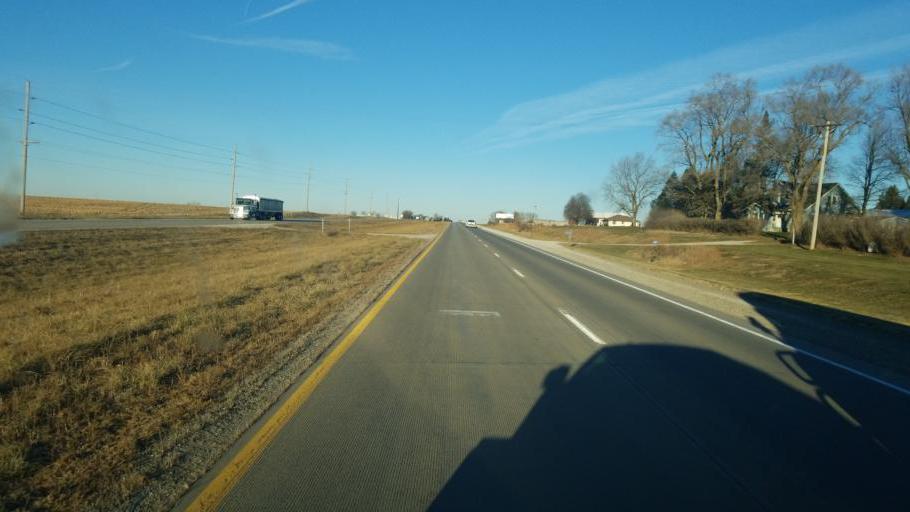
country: US
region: Iowa
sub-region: Marion County
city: Pella
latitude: 41.3735
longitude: -92.8063
